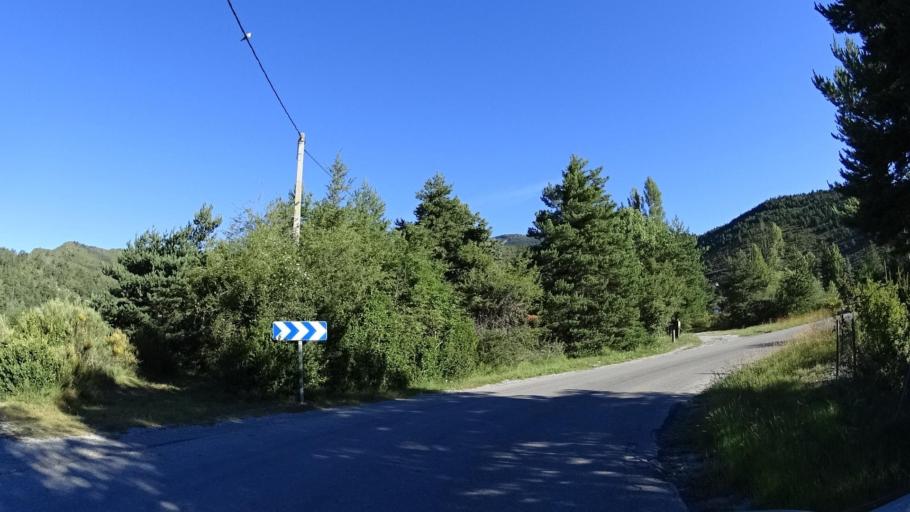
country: FR
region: Provence-Alpes-Cote d'Azur
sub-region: Departement des Alpes-de-Haute-Provence
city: Castellane
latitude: 43.8751
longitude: 6.5084
